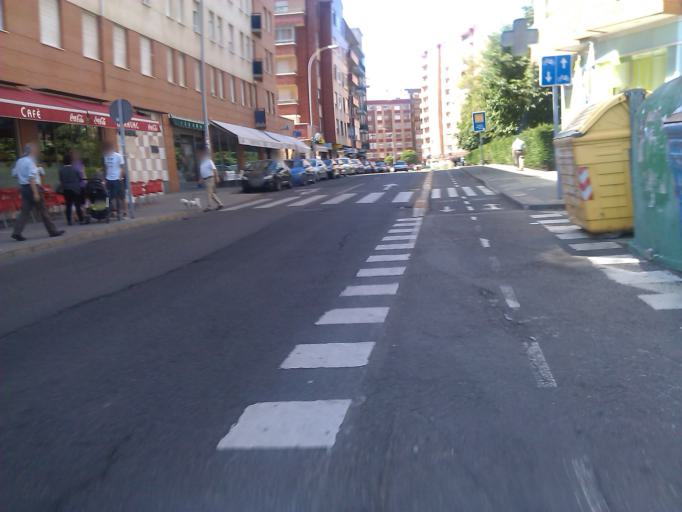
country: ES
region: Castille and Leon
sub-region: Provincia de Leon
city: Leon
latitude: 42.6077
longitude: -5.5662
